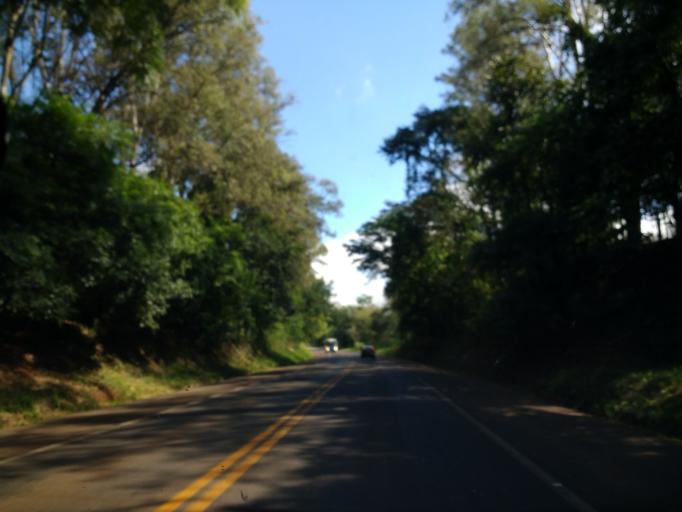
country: BR
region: Parana
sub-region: Umuarama
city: Umuarama
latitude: -23.7694
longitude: -53.2392
